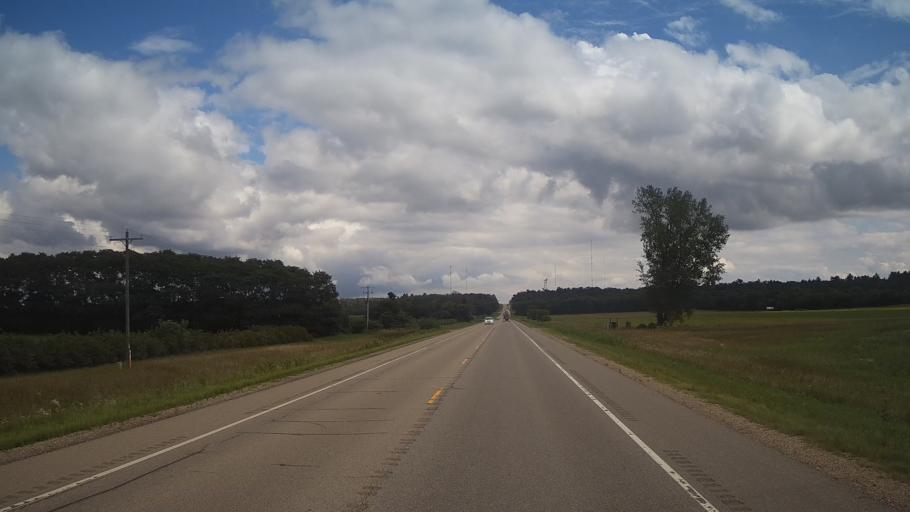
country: US
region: Wisconsin
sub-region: Marquette County
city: Westfield
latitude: 44.0220
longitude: -89.5891
